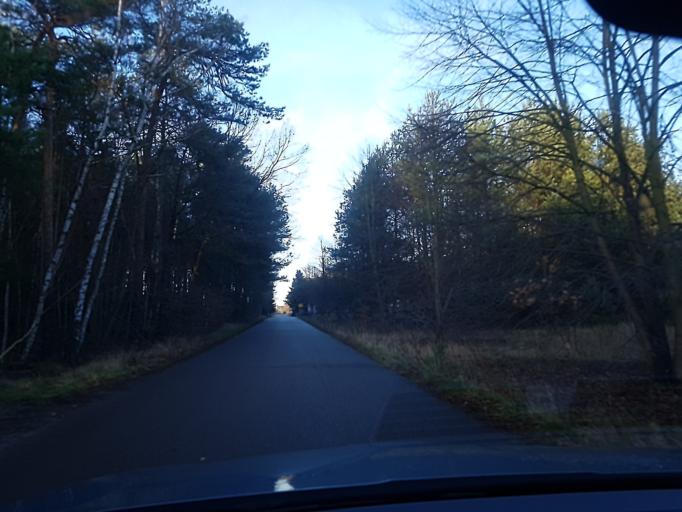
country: DE
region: Brandenburg
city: Schilda
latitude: 51.5988
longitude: 13.3868
